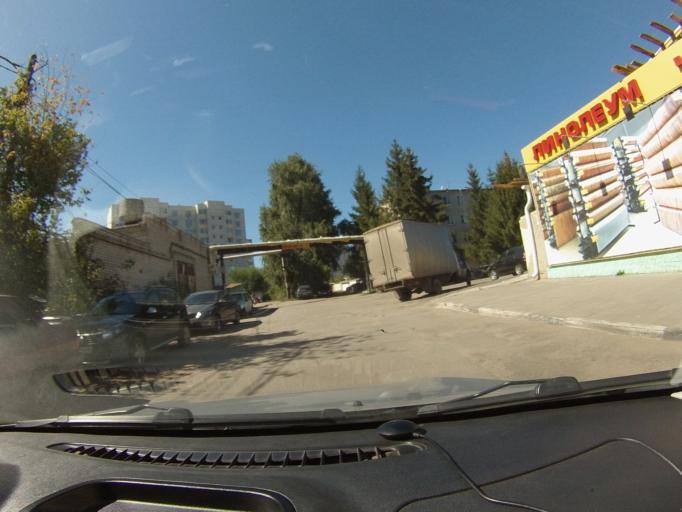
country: RU
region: Tambov
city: Tambov
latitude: 52.7593
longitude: 41.4333
